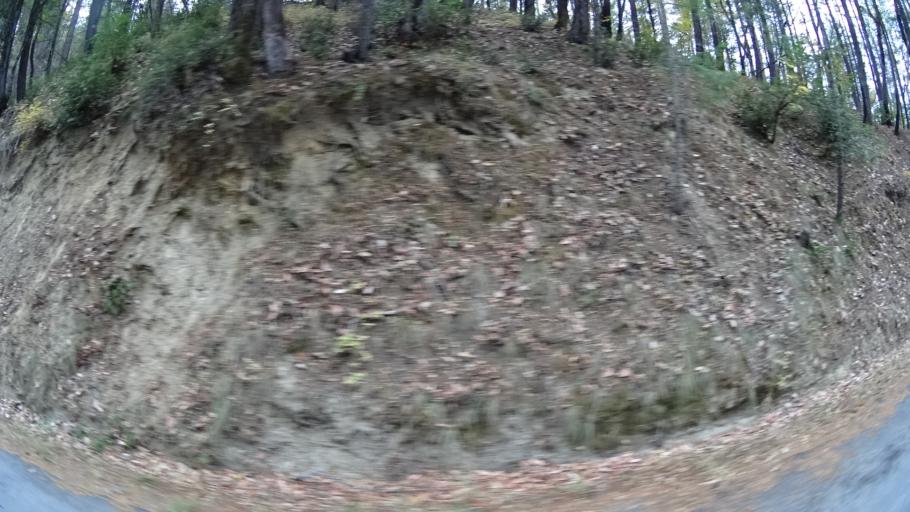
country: US
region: California
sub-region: Siskiyou County
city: Happy Camp
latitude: 41.8373
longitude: -123.1997
